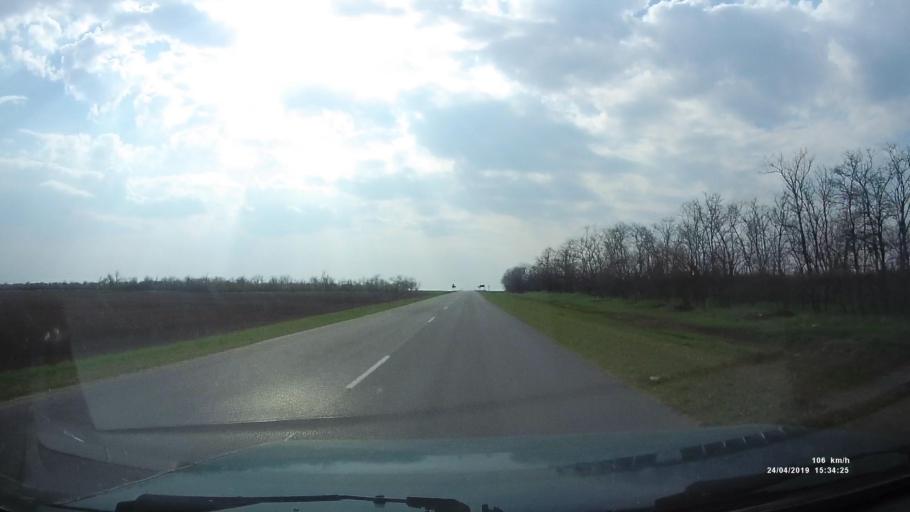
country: RU
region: Kalmykiya
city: Yashalta
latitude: 46.5998
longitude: 42.9161
